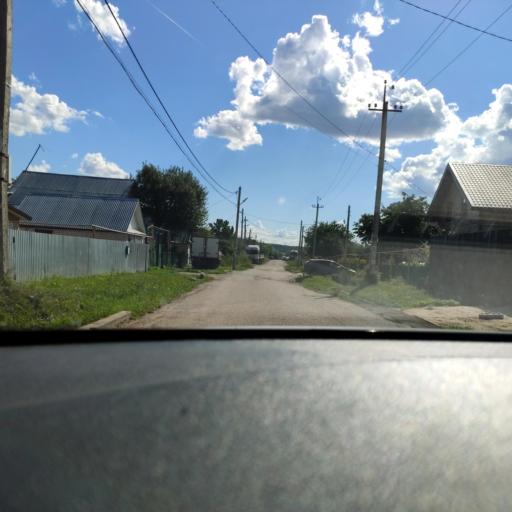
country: RU
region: Tatarstan
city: Vysokaya Gora
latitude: 55.8756
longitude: 49.2545
